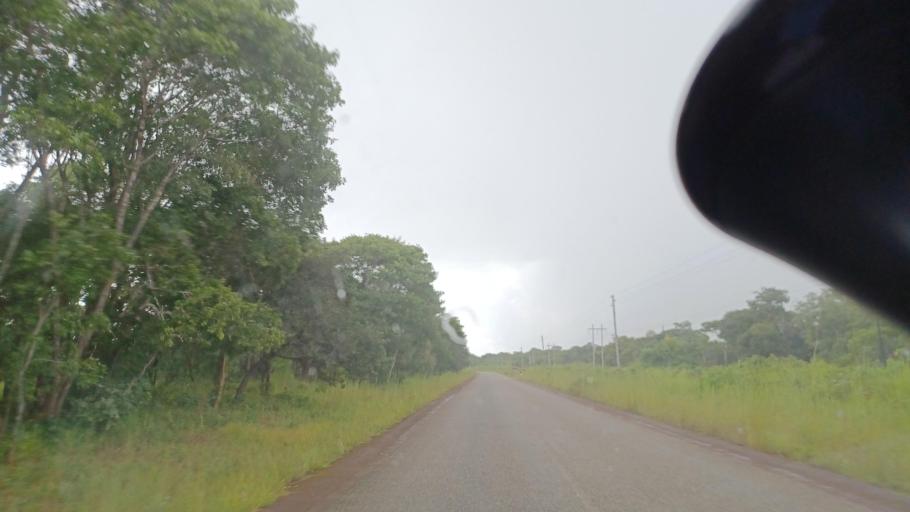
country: ZM
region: North-Western
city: Kasempa
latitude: -13.0918
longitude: 25.9285
